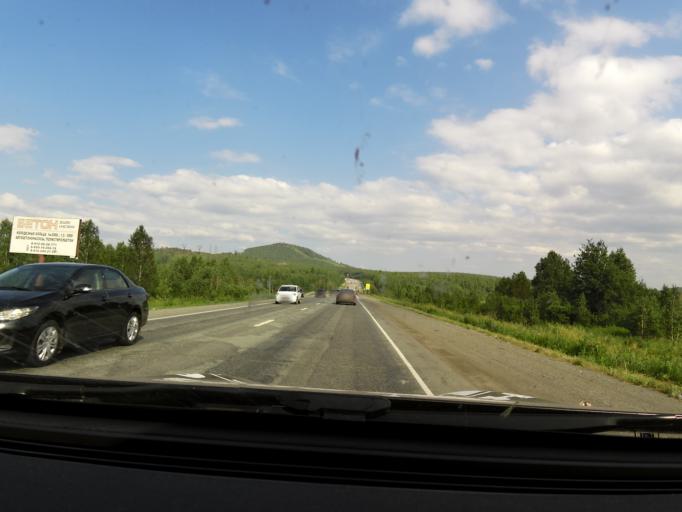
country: RU
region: Sverdlovsk
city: Revda
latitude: 56.8268
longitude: 59.9627
